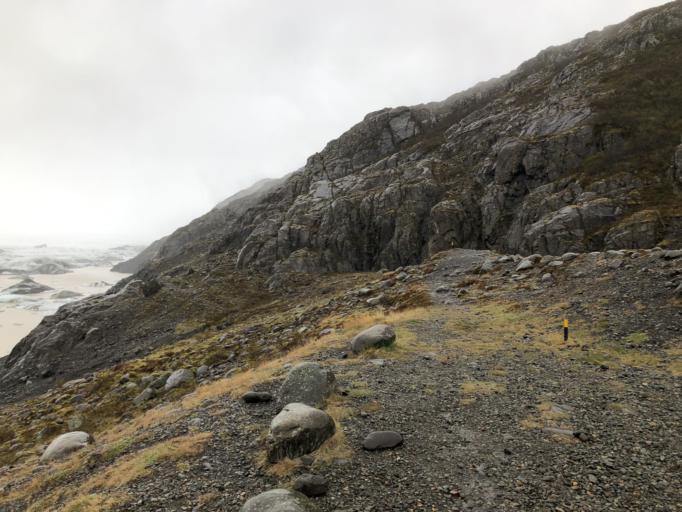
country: IS
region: East
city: Hoefn
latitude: 64.4189
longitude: -15.3987
